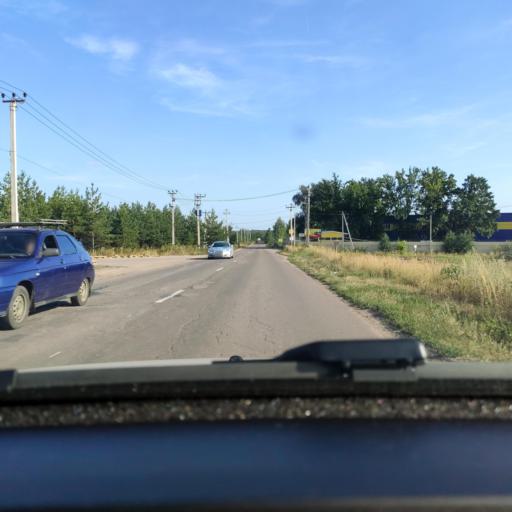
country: RU
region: Voronezj
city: Podgornoye
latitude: 51.8318
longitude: 39.2050
